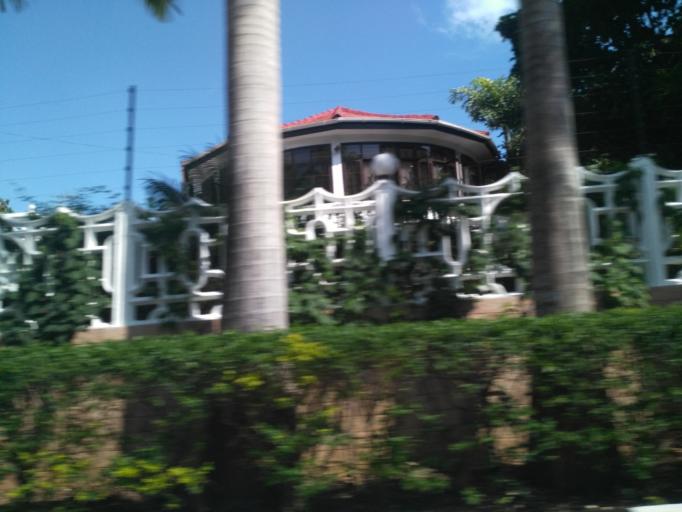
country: TZ
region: Dar es Salaam
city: Magomeni
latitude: -6.7486
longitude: 39.2810
